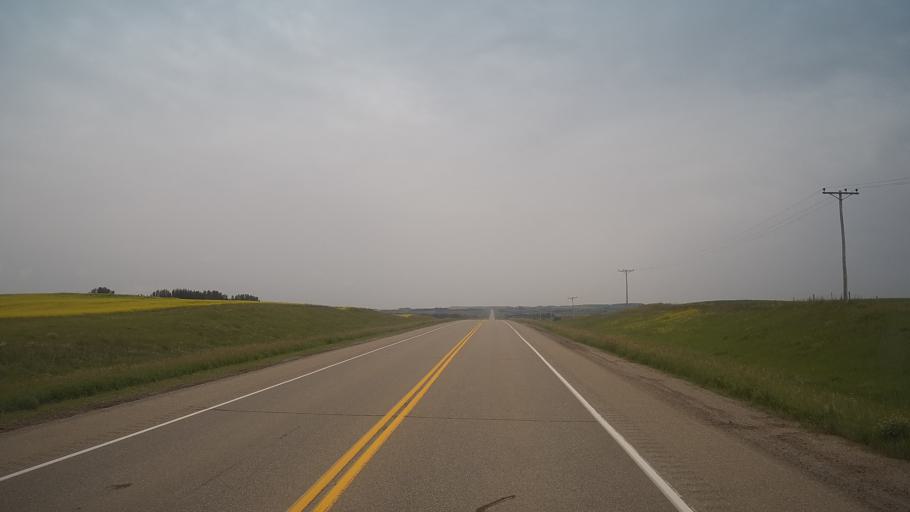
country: CA
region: Saskatchewan
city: Biggar
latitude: 52.0564
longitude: -107.7921
